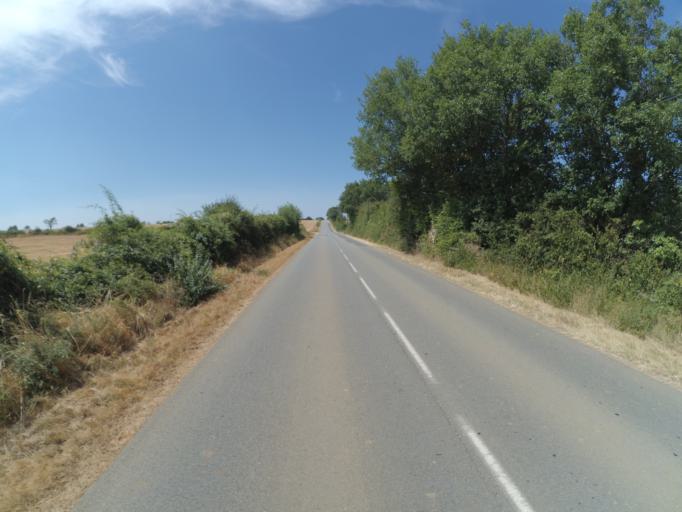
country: FR
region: Poitou-Charentes
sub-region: Departement de la Vienne
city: Vivonne
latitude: 46.4216
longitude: 0.2967
